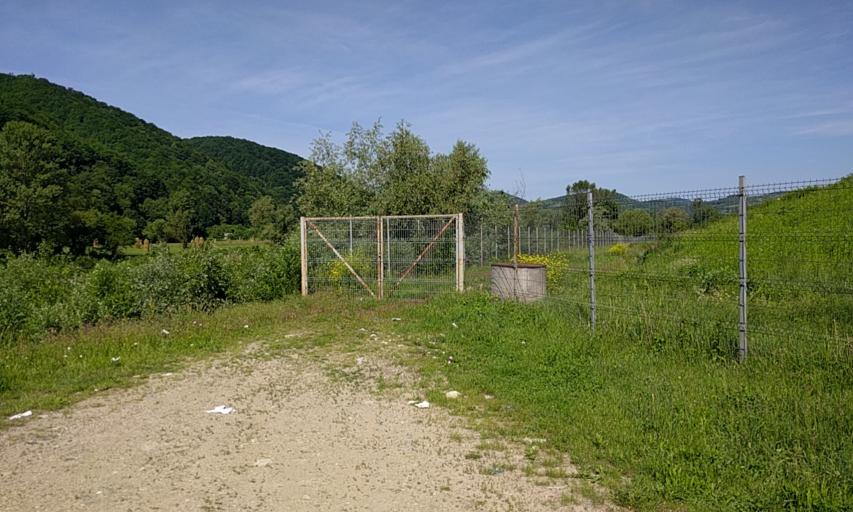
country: RO
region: Bistrita-Nasaud
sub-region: Oras Nasaud
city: Nasaud
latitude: 47.2929
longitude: 24.3770
